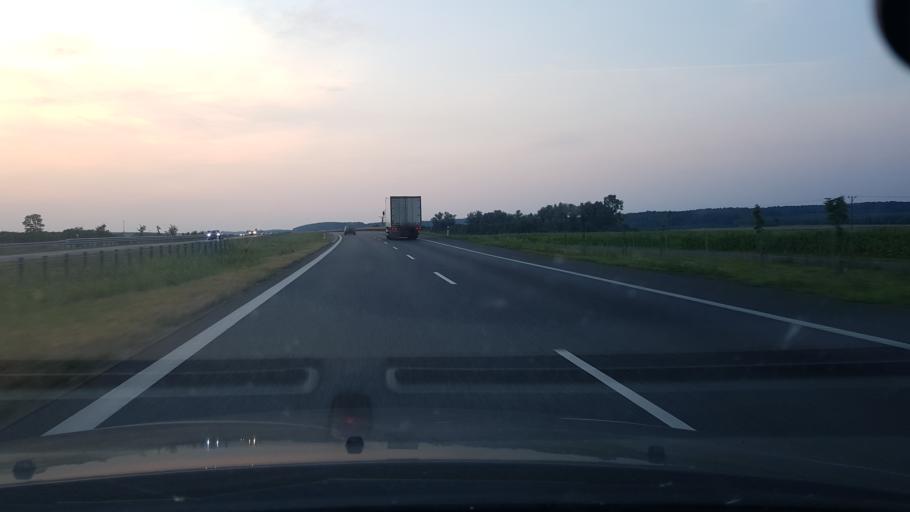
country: PL
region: Warmian-Masurian Voivodeship
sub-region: Powiat nidzicki
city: Nidzica
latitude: 53.3936
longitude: 20.3655
